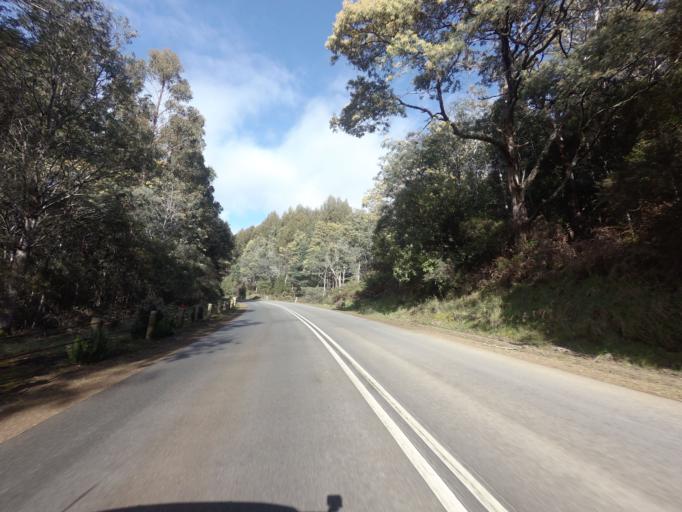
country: AU
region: Tasmania
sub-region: Huon Valley
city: Geeveston
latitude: -43.3438
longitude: 146.9622
